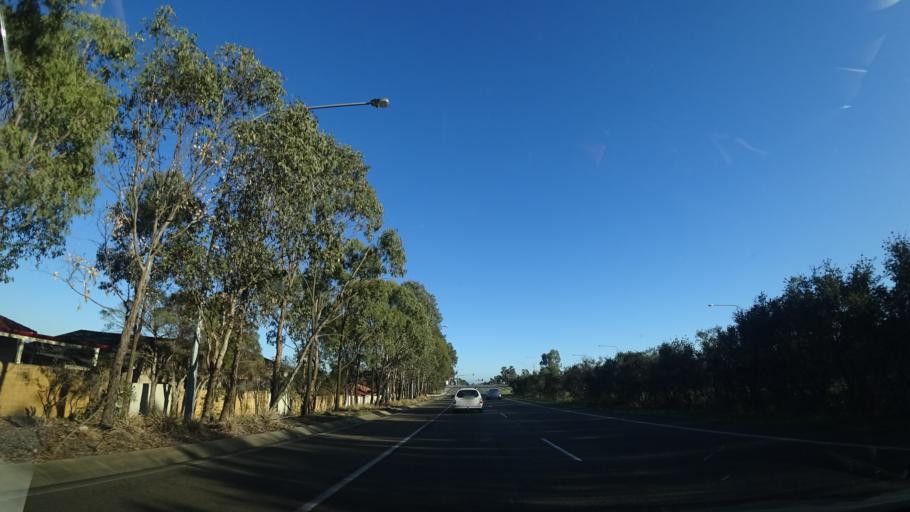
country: AU
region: New South Wales
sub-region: Blacktown
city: Stanhope Gardens
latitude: -33.7275
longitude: 150.9409
